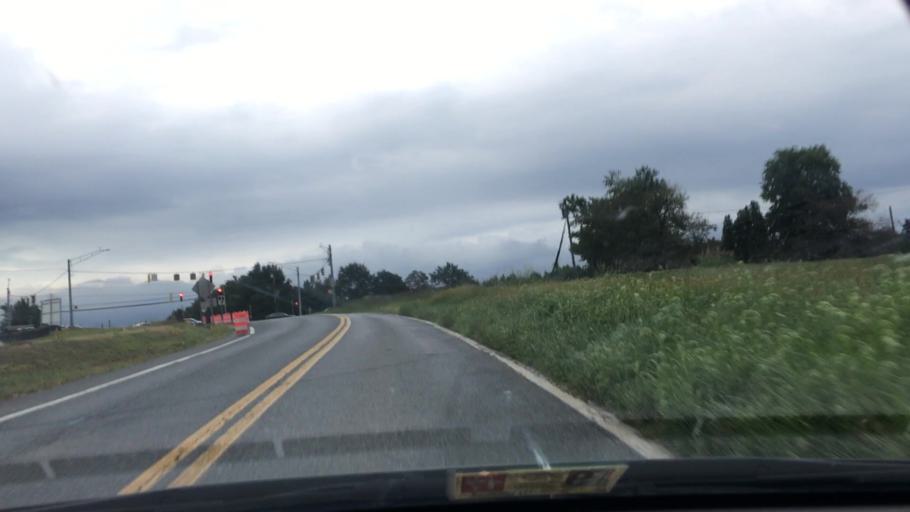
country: US
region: Maryland
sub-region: Montgomery County
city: Clarksburg
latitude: 39.2105
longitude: -77.2415
